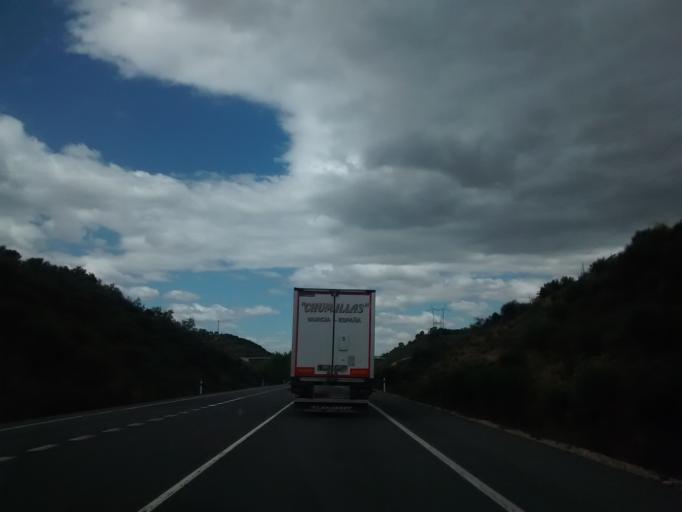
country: ES
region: La Rioja
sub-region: Provincia de La Rioja
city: Ausejo
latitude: 42.3333
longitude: -2.1582
